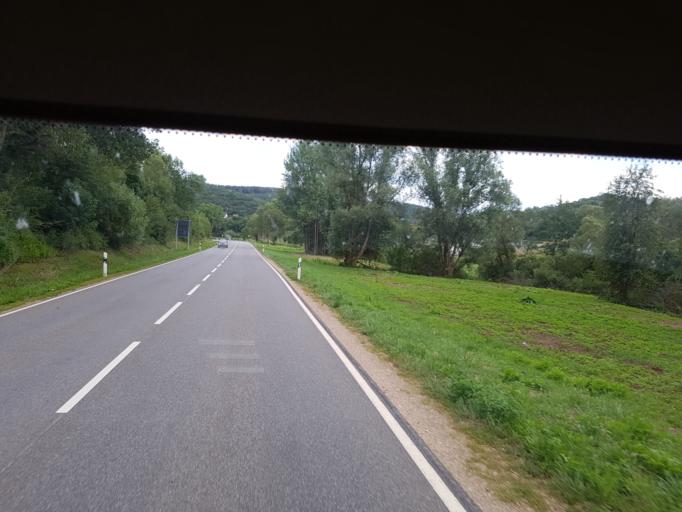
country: DE
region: Rheinland-Pfalz
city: Gerolstein
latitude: 50.2159
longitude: 6.6281
